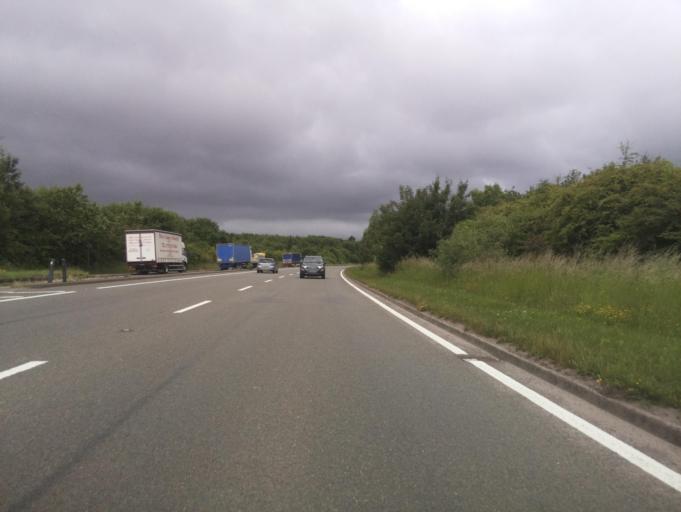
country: GB
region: England
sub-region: Leicestershire
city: Ashby de la Zouch
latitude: 52.7621
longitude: -1.4853
